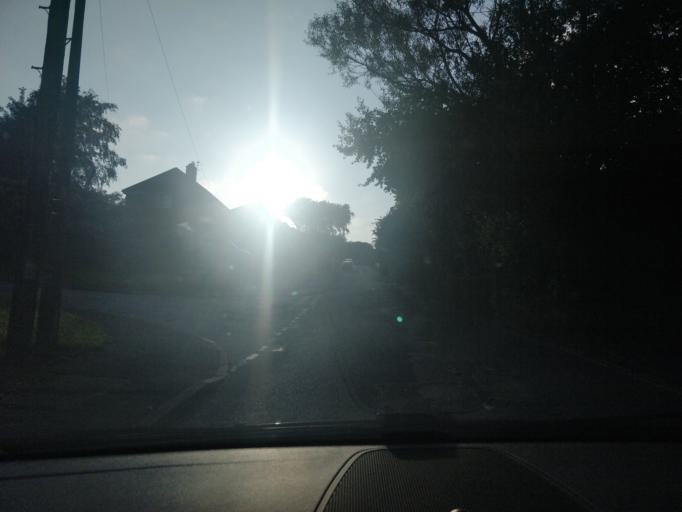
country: GB
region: England
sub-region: Lancashire
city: Appley Bridge
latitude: 53.5438
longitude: -2.7310
